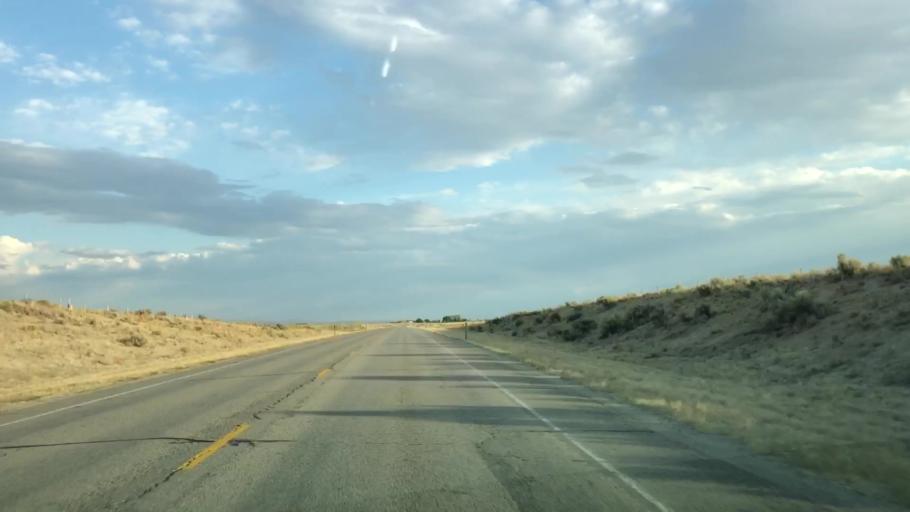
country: US
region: Wyoming
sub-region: Sweetwater County
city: North Rock Springs
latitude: 42.0964
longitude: -109.4439
